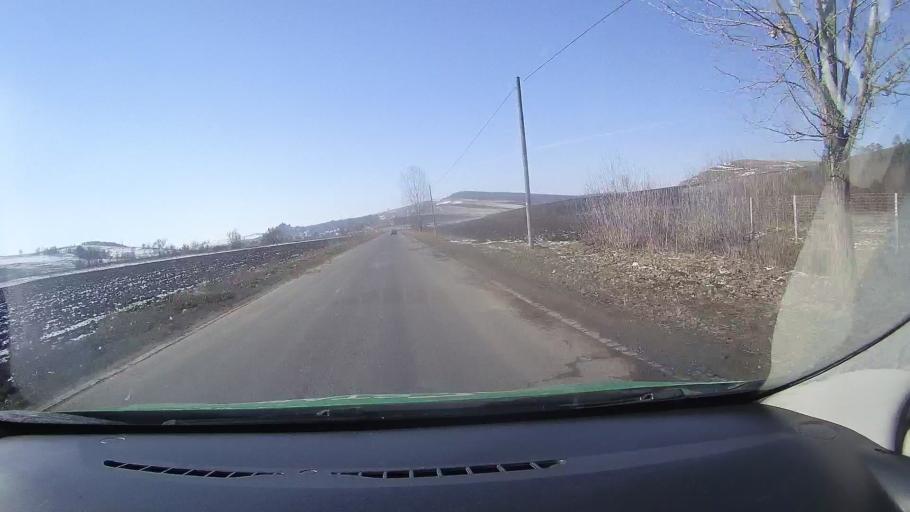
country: RO
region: Brasov
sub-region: Comuna Homorod
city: Homorod
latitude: 46.0401
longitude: 25.2550
